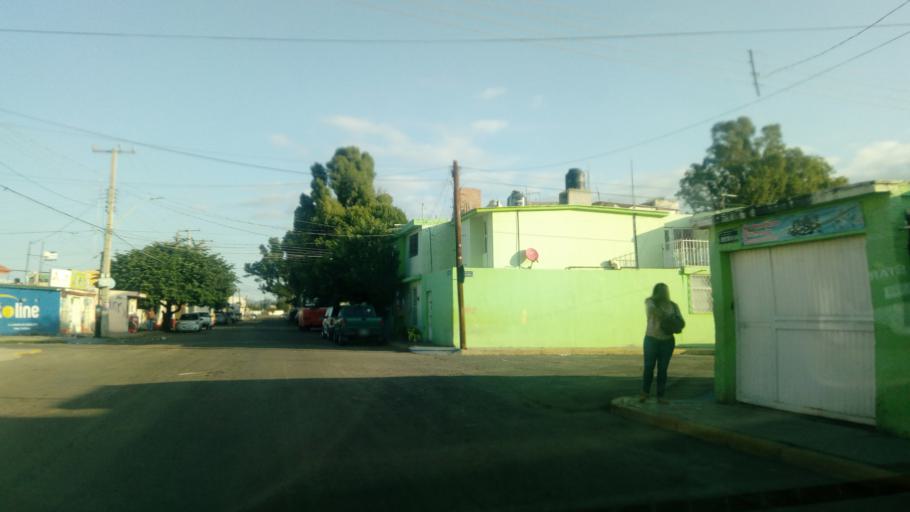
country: MX
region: Durango
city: Victoria de Durango
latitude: 24.0477
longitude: -104.6189
